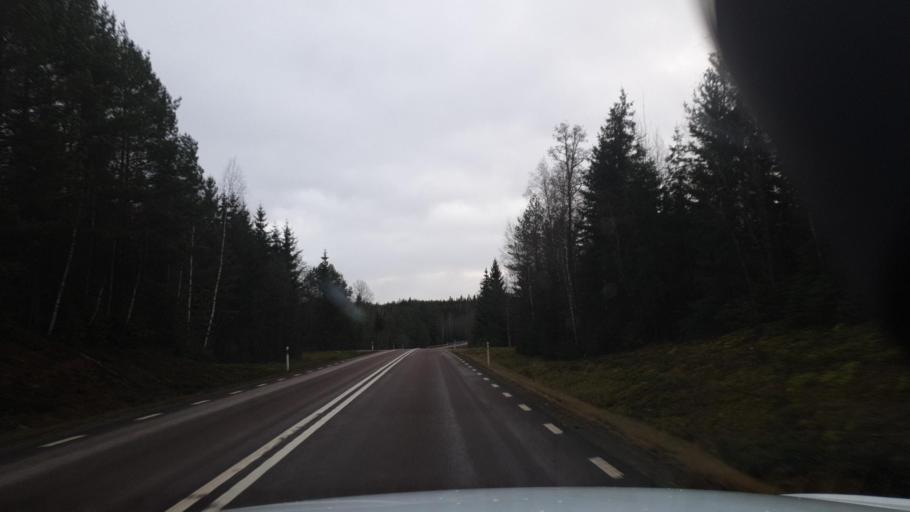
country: SE
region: Vaermland
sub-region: Arvika Kommun
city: Arvika
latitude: 59.7240
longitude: 12.5123
